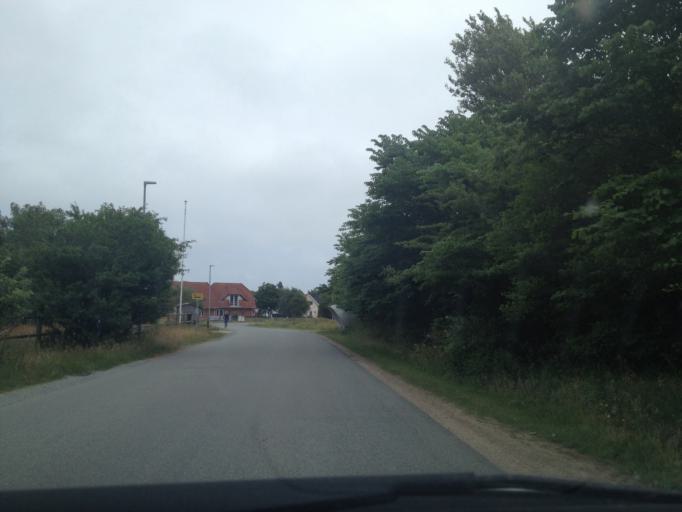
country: DK
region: South Denmark
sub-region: Varde Kommune
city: Oksbol
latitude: 55.5489
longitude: 8.2258
